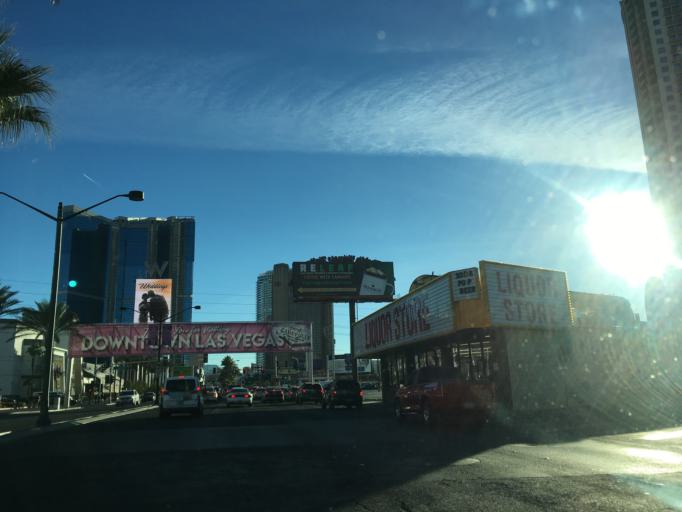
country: US
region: Nevada
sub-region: Clark County
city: Las Vegas
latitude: 36.1447
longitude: -115.1568
